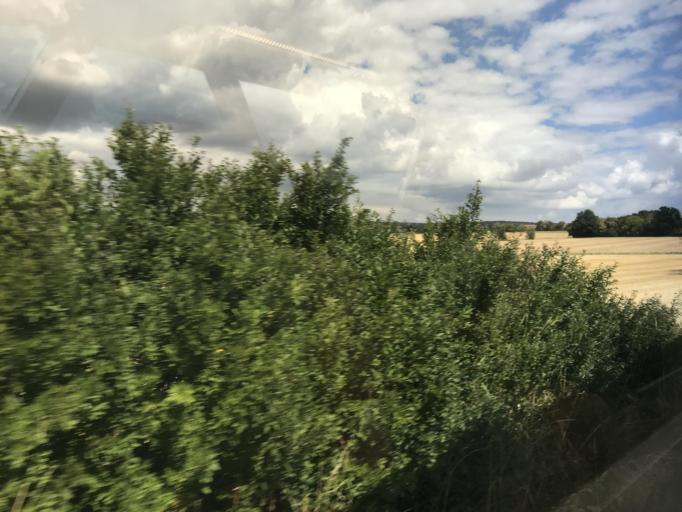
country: DE
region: Bavaria
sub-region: Regierungsbezirk Unterfranken
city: Elfershausen
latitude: 50.1433
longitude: 9.9908
